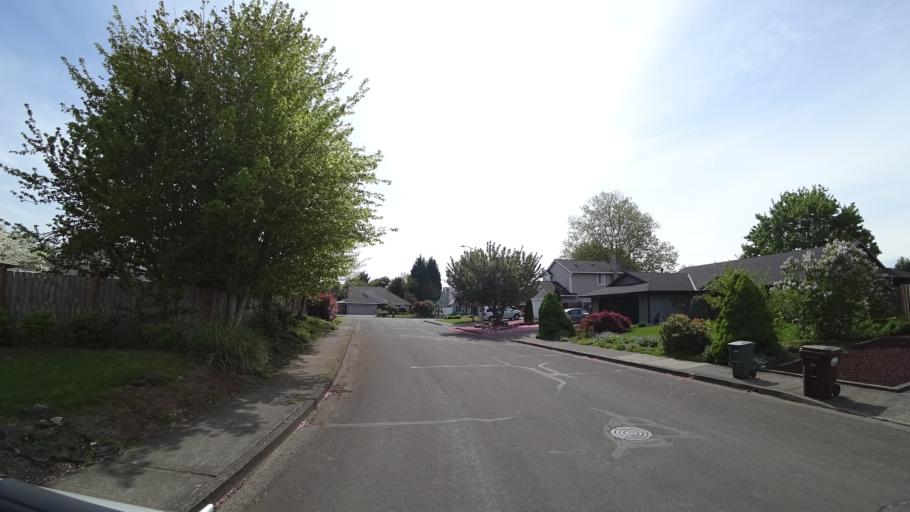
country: US
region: Oregon
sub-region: Washington County
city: Rockcreek
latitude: 45.5355
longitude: -122.9281
